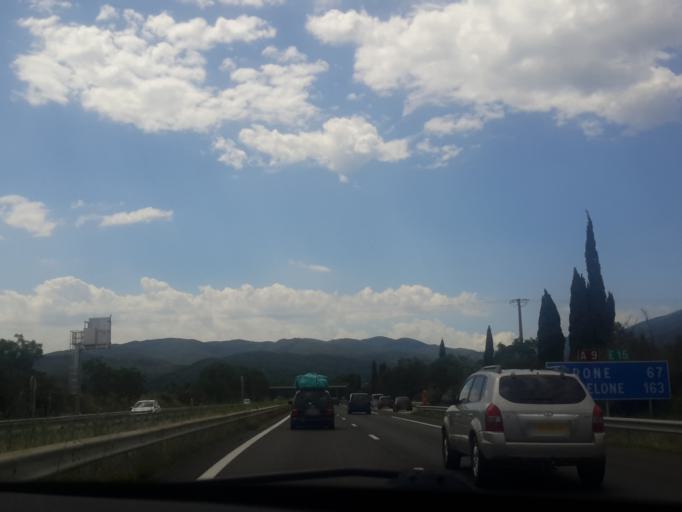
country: FR
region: Languedoc-Roussillon
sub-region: Departement des Pyrenees-Orientales
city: el Volo
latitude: 42.5133
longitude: 2.8184
